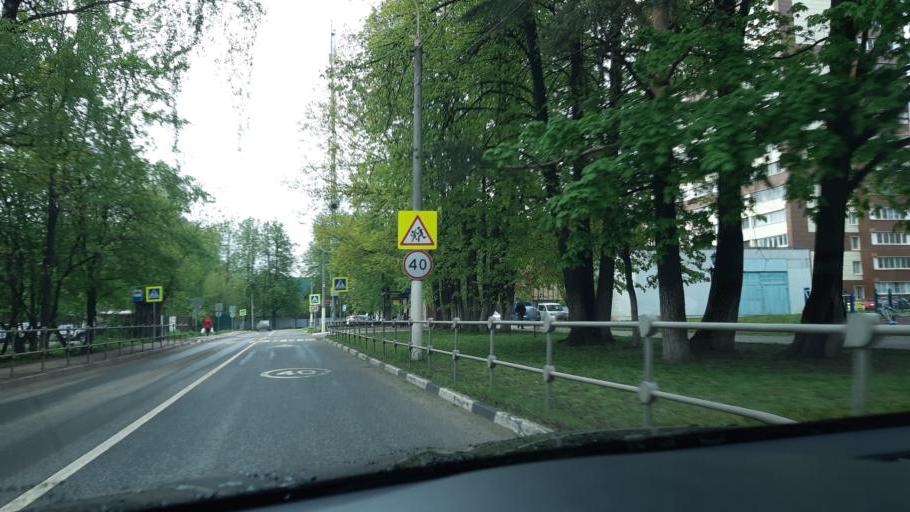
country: RU
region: Moskovskaya
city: Dolgoprudnyy
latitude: 55.9521
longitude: 37.4913
